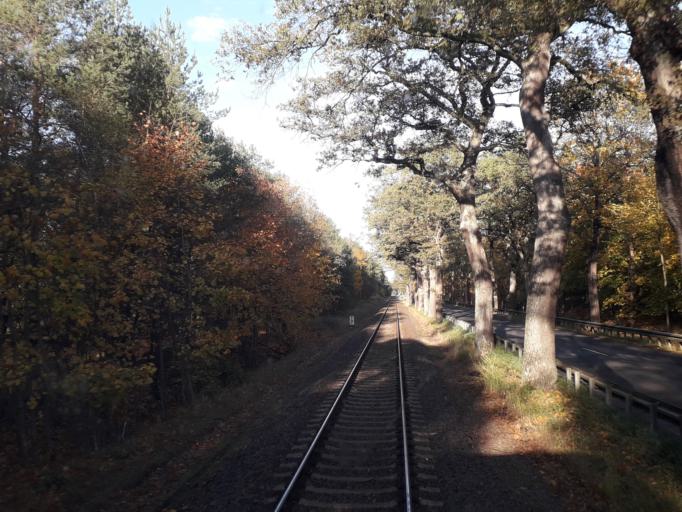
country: DE
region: Brandenburg
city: Perleberg
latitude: 53.0523
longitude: 11.8281
